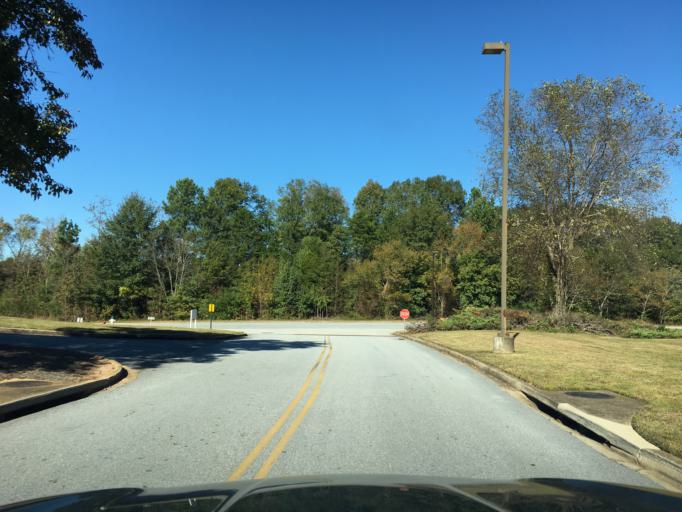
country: US
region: South Carolina
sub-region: Spartanburg County
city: Wellford
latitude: 34.9127
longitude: -82.0977
